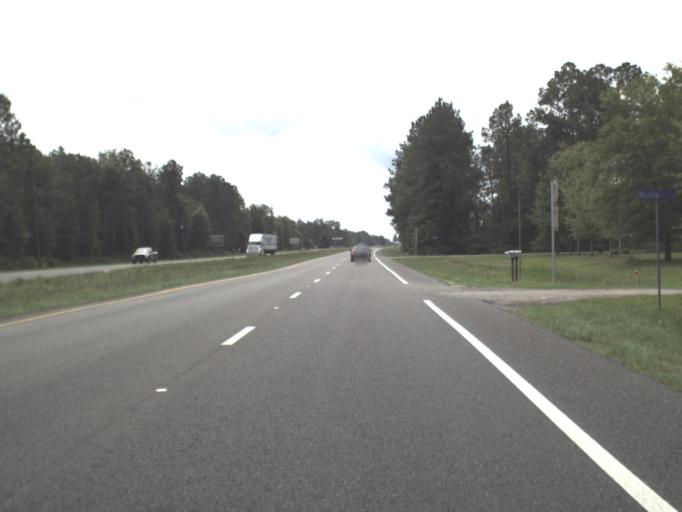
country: US
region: Florida
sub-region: Nassau County
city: Hilliard
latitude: 30.7414
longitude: -81.9531
